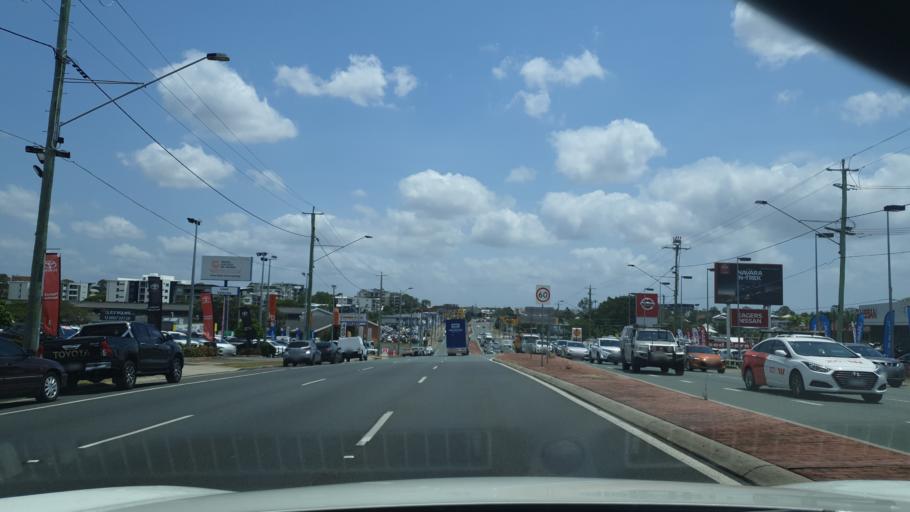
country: AU
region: Queensland
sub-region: Brisbane
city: Wavell Heights
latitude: -27.3995
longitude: 153.0315
